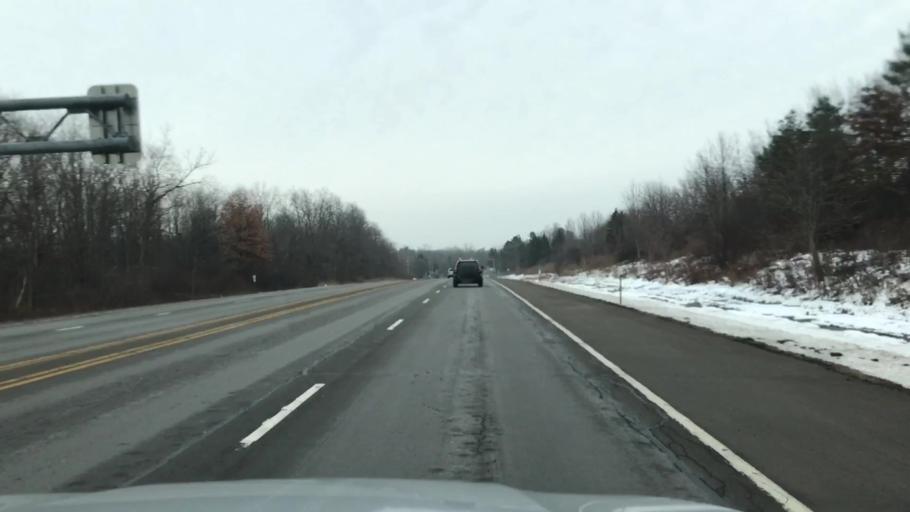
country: US
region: New York
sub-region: Erie County
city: Orchard Park
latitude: 42.7490
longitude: -78.7539
